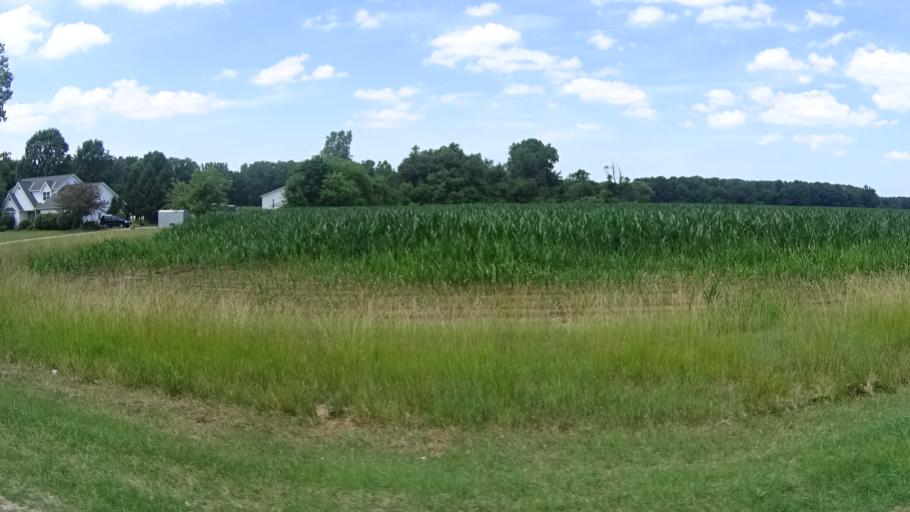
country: US
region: Ohio
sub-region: Erie County
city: Milan
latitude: 41.3021
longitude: -82.5291
